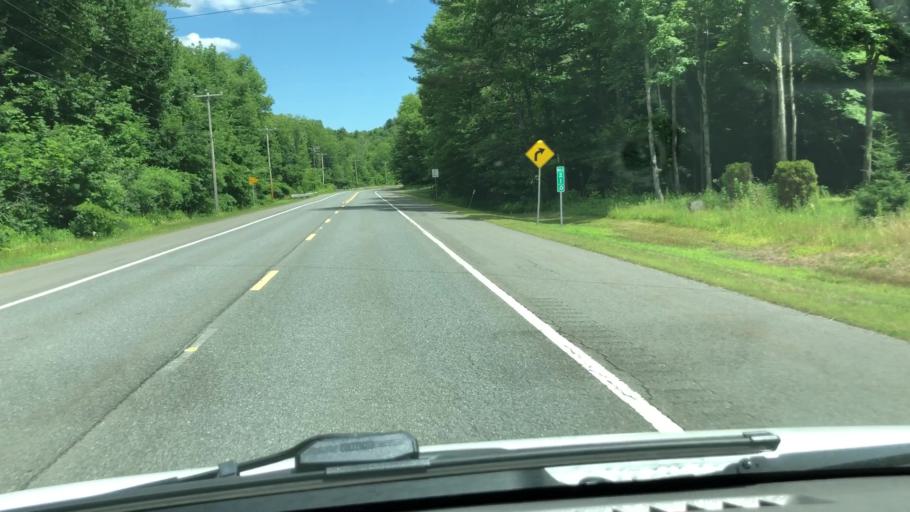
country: US
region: Massachusetts
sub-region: Hampshire County
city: Chesterfield
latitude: 42.4729
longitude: -72.9154
